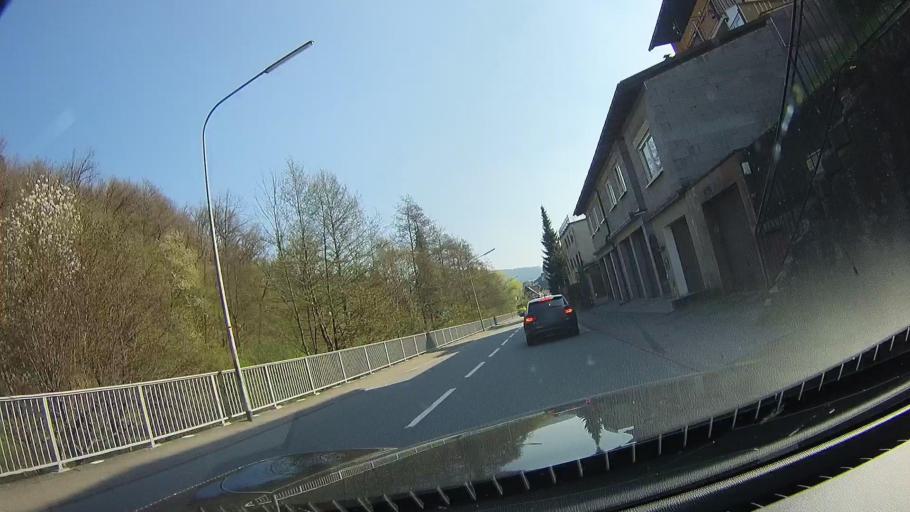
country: DE
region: Hesse
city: Hirschhorn
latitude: 49.4531
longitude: 8.8947
